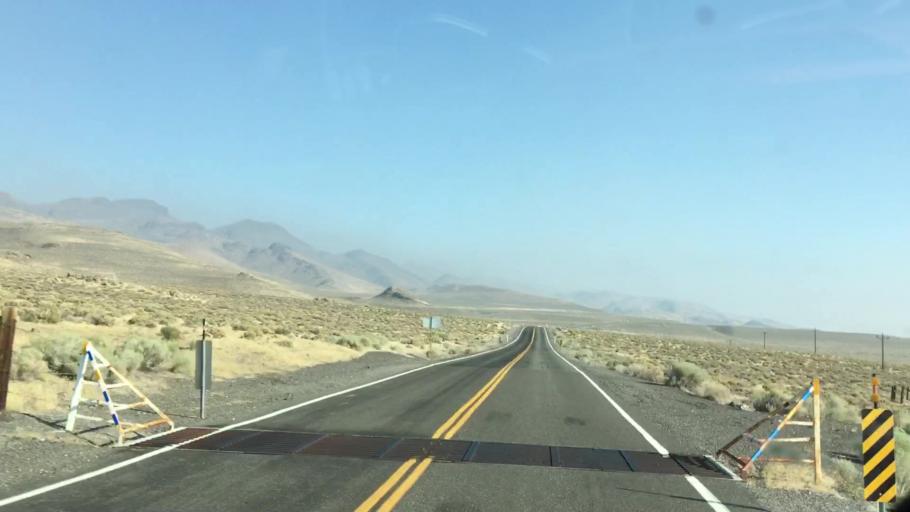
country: US
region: Nevada
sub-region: Lyon County
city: Fernley
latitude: 39.9893
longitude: -119.3865
